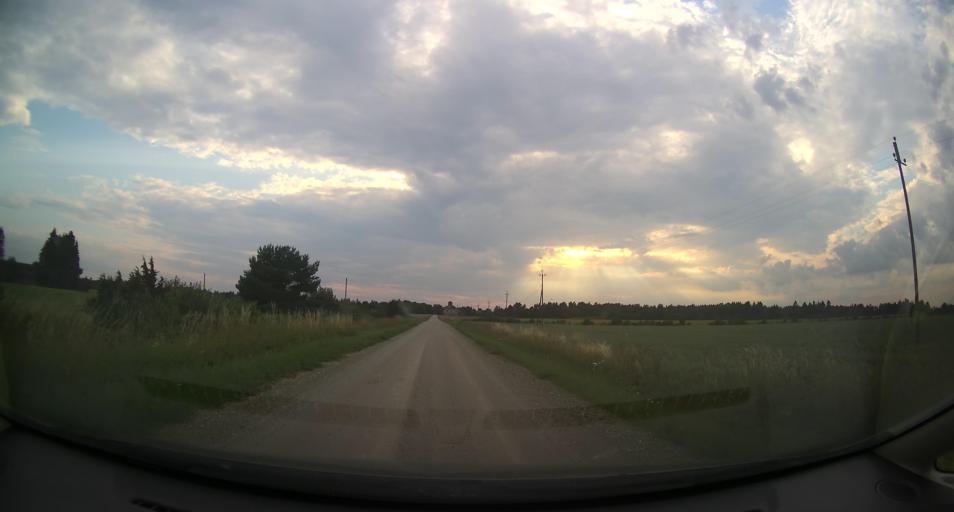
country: EE
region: Laeaene
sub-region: Lihula vald
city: Lihula
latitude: 58.5674
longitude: 23.6790
